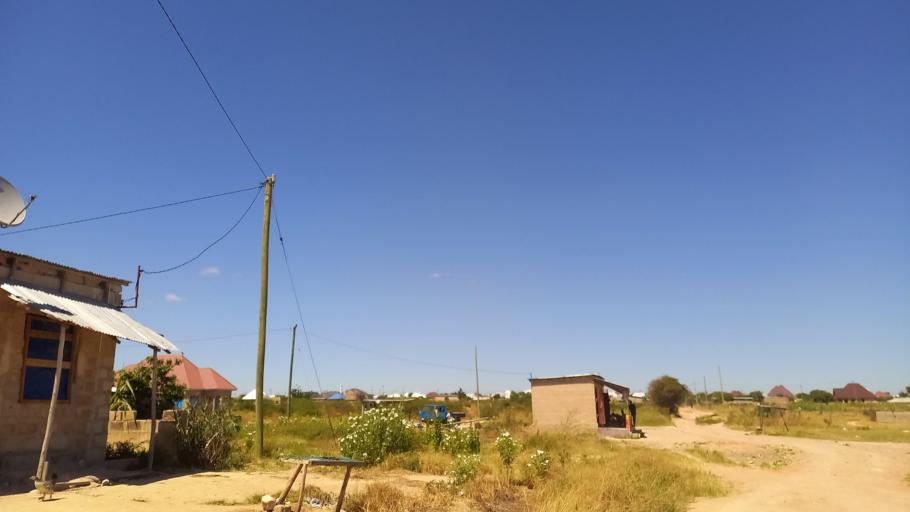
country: TZ
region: Dodoma
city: Dodoma
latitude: -6.1251
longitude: 35.6969
